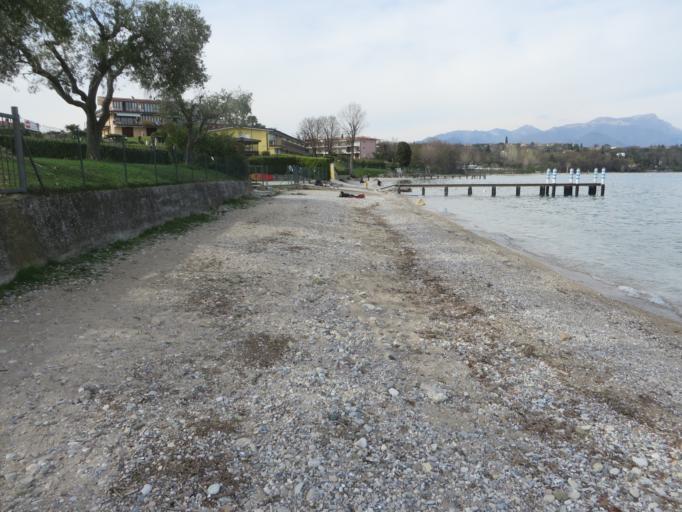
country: IT
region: Lombardy
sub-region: Provincia di Brescia
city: Manerba del Garda
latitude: 45.5328
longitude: 10.5574
